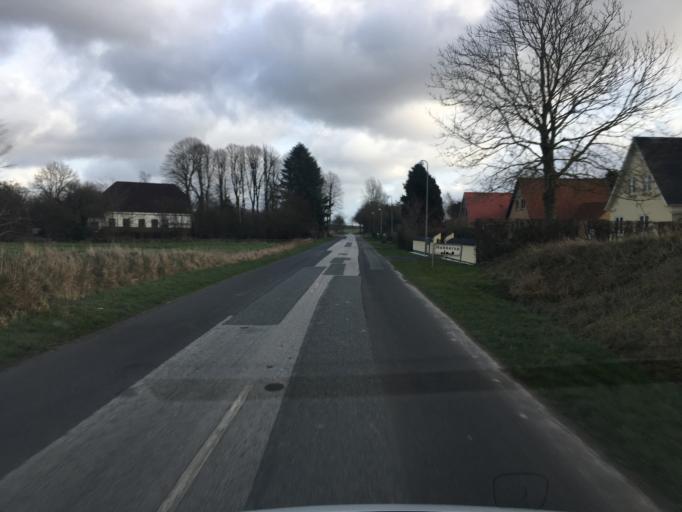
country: DE
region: Schleswig-Holstein
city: Wees
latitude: 54.8955
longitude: 9.4865
